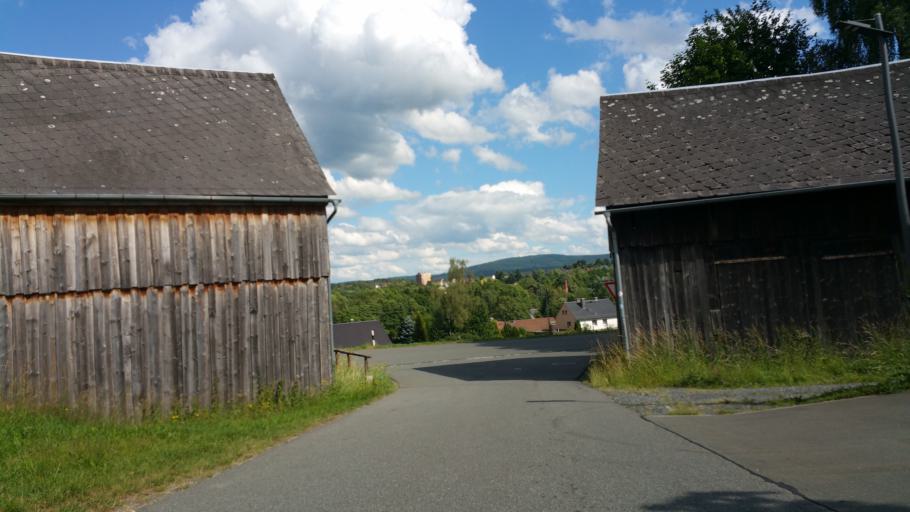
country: DE
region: Bavaria
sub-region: Upper Franconia
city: Schwarzenbach an der Saale
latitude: 50.2268
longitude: 11.9312
